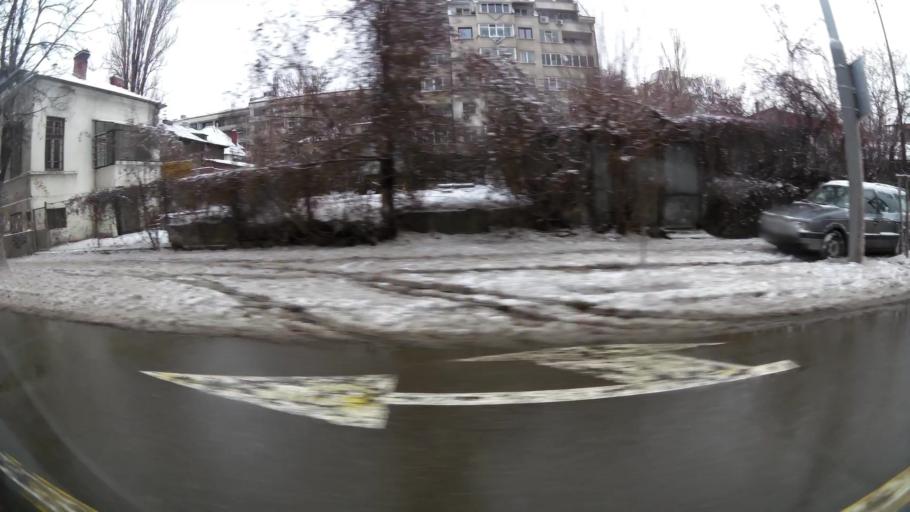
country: BG
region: Sofia-Capital
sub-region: Stolichna Obshtina
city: Sofia
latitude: 42.7064
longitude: 23.3082
